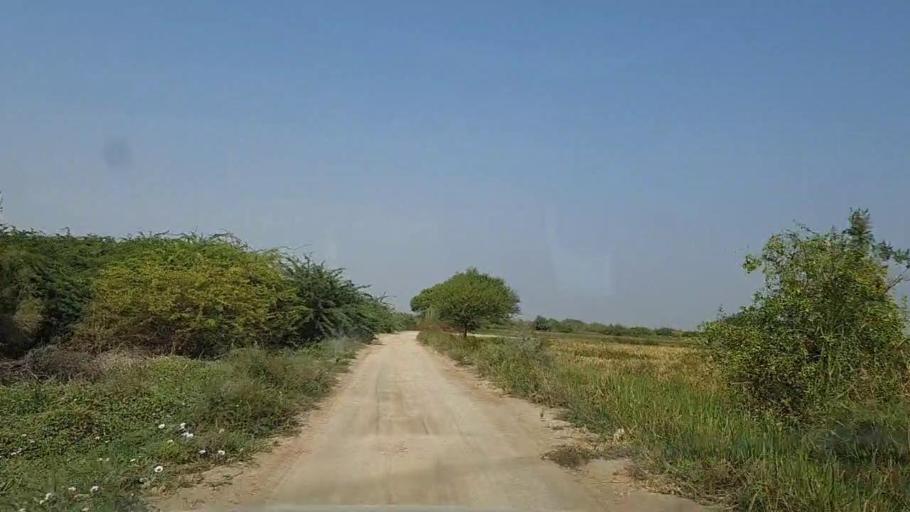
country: PK
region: Sindh
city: Mirpur Sakro
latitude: 24.5530
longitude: 67.5589
